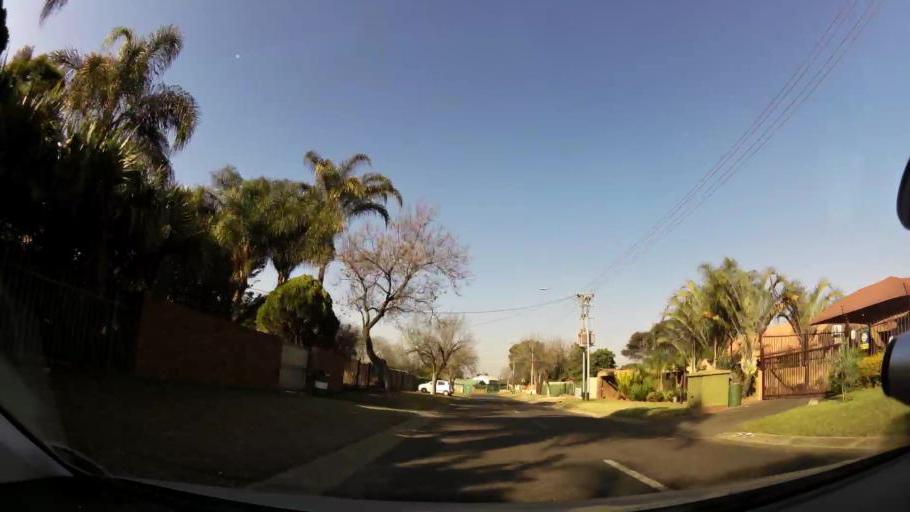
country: ZA
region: Gauteng
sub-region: City of Tshwane Metropolitan Municipality
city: Pretoria
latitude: -25.7225
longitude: 28.1520
